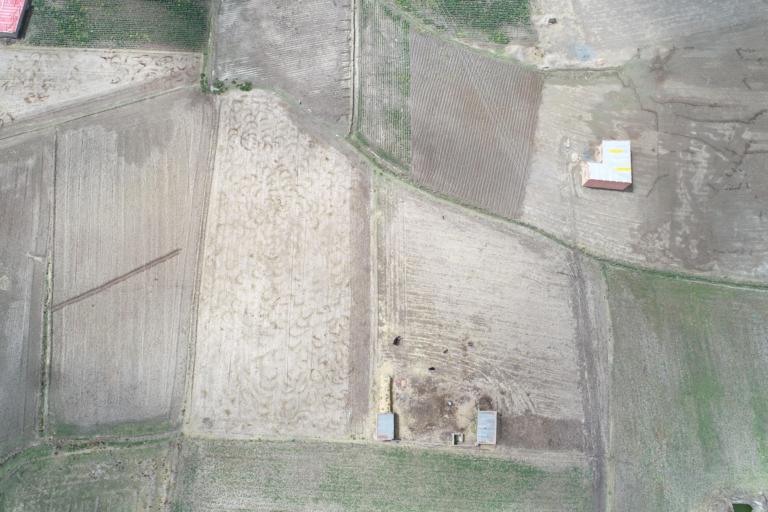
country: BO
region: La Paz
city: Achacachi
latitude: -16.0305
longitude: -68.6864
